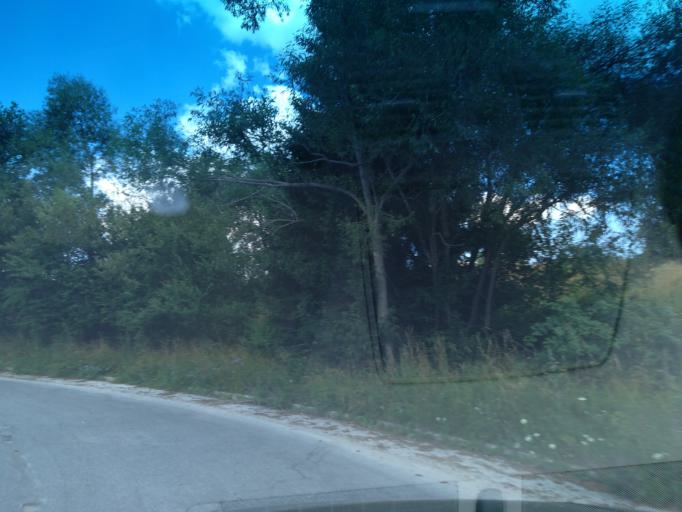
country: BG
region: Smolyan
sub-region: Obshtina Chepelare
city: Chepelare
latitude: 41.6694
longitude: 24.7770
